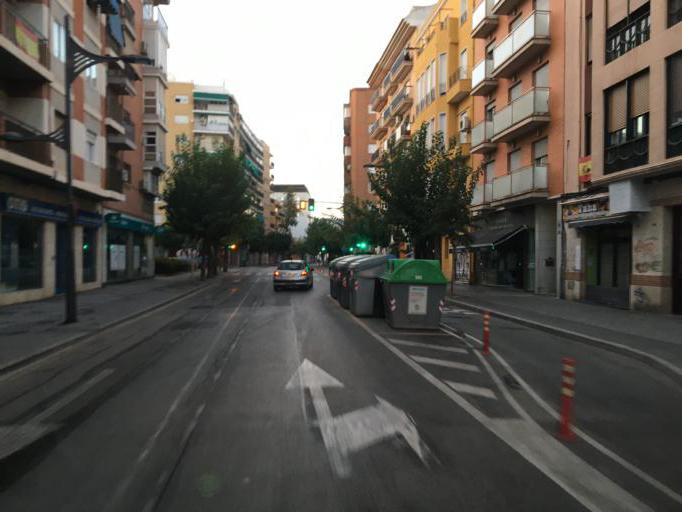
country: ES
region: Murcia
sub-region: Murcia
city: Murcia
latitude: 37.9845
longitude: -1.1229
